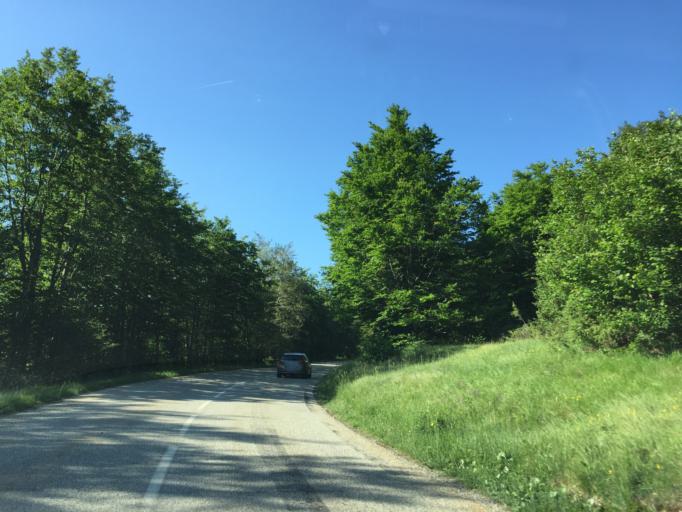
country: FR
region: Rhone-Alpes
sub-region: Departement de la Drome
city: Saint-Laurent-en-Royans
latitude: 44.9343
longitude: 5.3842
